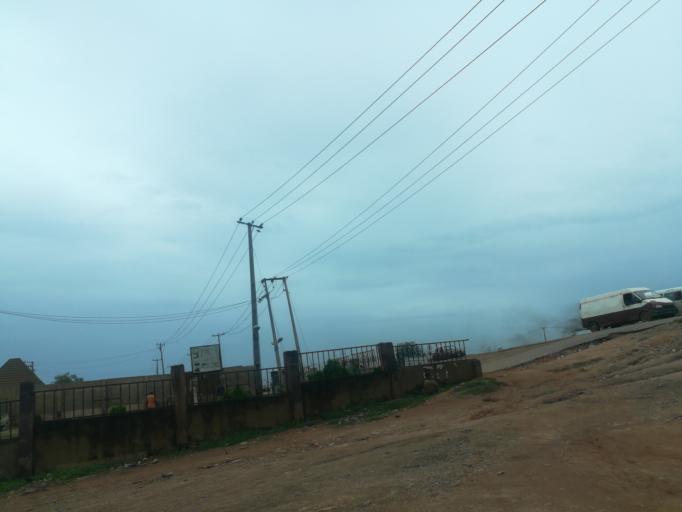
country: NG
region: Oyo
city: Ibadan
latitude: 7.3403
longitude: 3.9077
